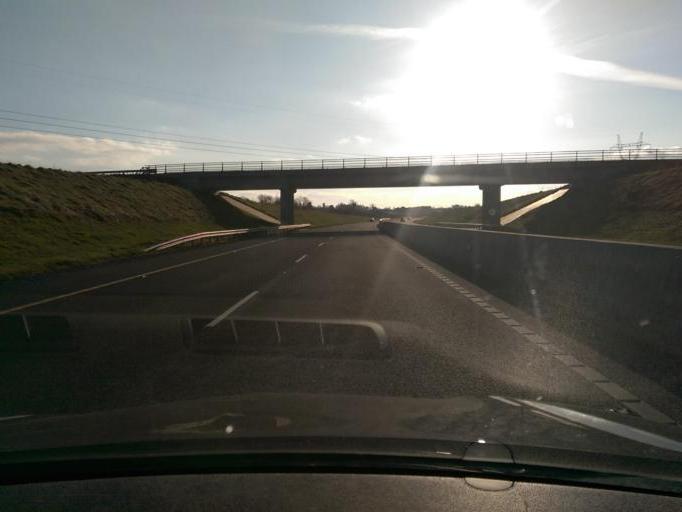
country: IE
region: Leinster
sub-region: Laois
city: Mountrath
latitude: 52.9149
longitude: -7.4949
